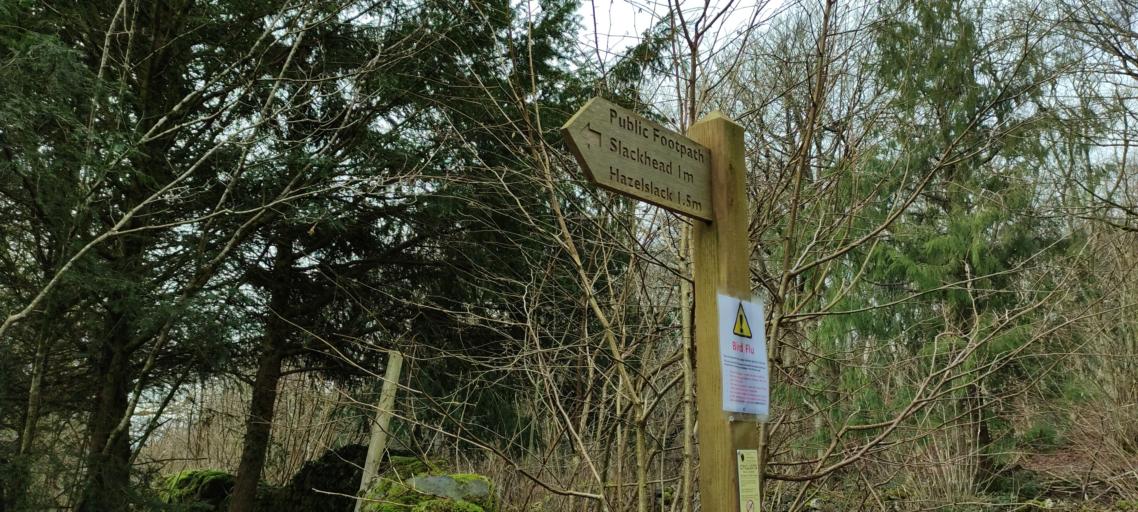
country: GB
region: England
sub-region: Cumbria
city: Milnthorpe
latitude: 54.2124
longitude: -2.7938
